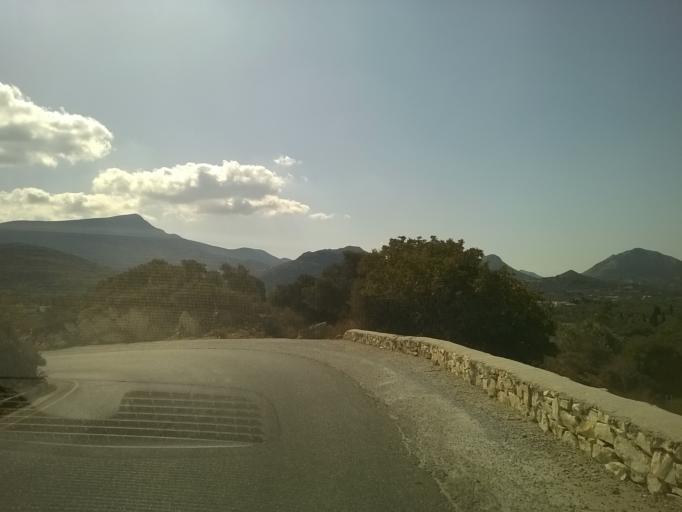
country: GR
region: South Aegean
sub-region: Nomos Kykladon
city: Filotion
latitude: 37.0725
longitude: 25.4878
